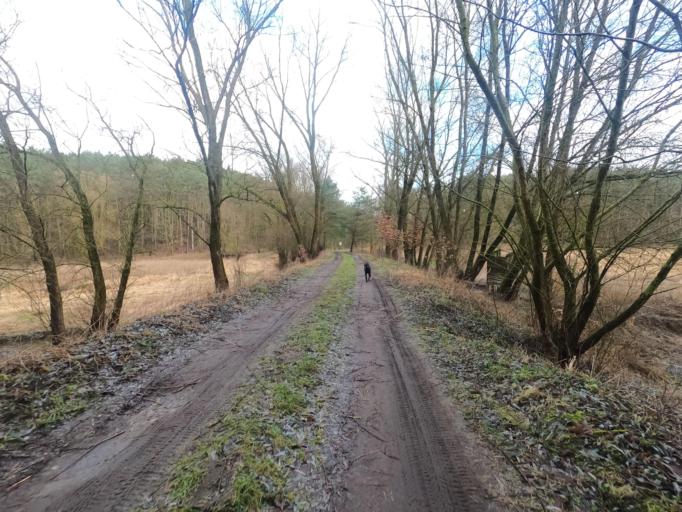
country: PL
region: Greater Poland Voivodeship
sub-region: Powiat pilski
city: Smilowo
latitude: 53.1111
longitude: 16.9136
